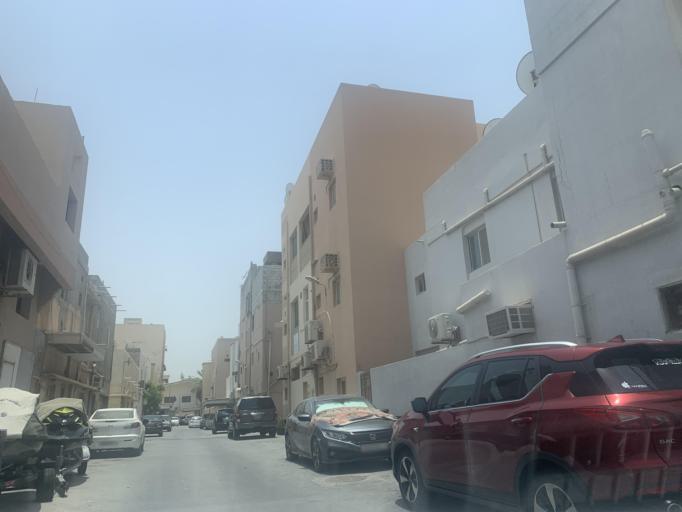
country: BH
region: Manama
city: Jidd Hafs
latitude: 26.2166
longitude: 50.4596
